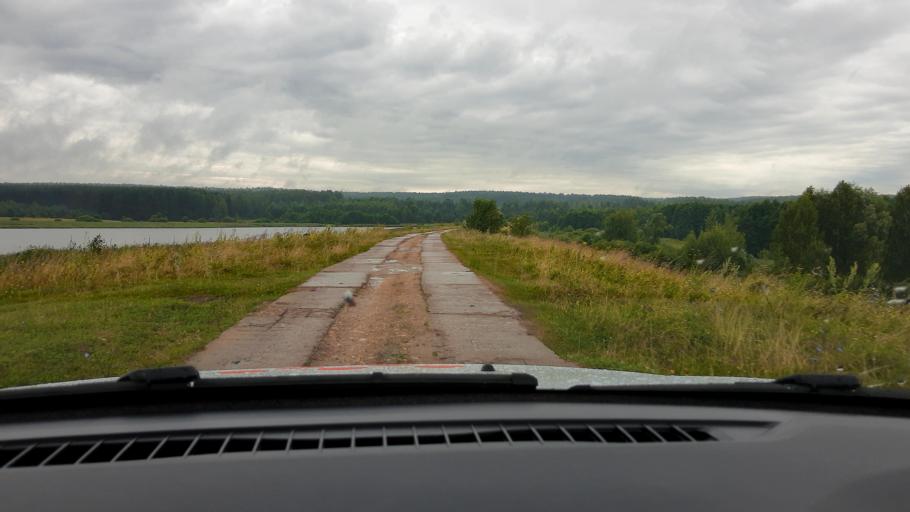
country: RU
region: Nizjnij Novgorod
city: Surovatikha
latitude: 55.9343
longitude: 43.9174
